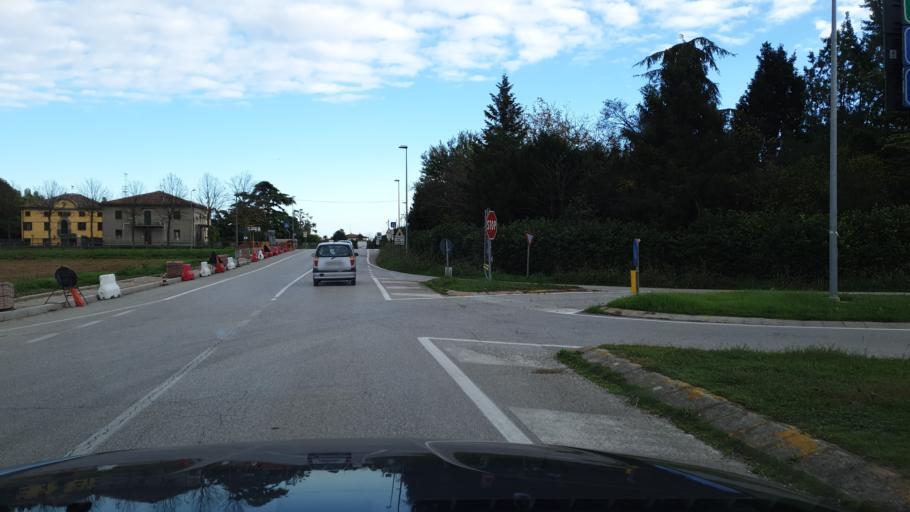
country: IT
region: Veneto
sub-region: Provincia di Rovigo
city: Fratta Polesine
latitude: 45.0276
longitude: 11.6399
